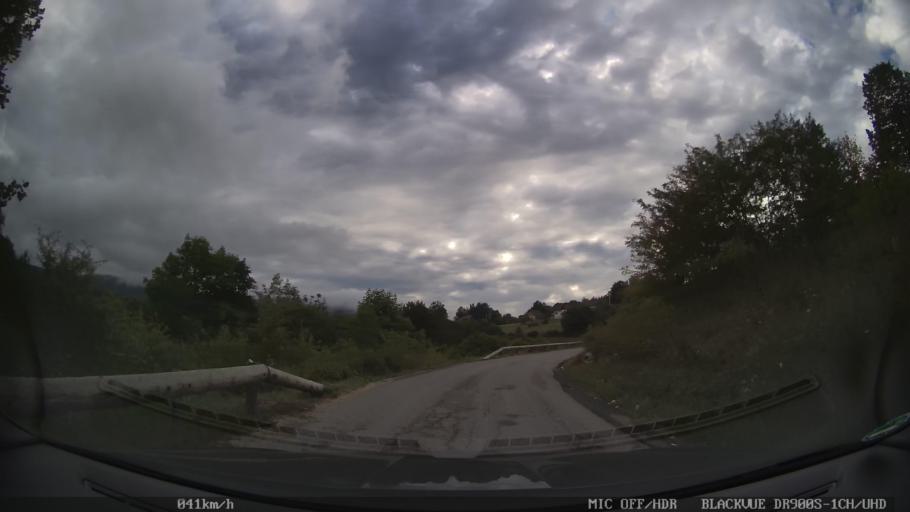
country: HR
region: Licko-Senjska
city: Jezerce
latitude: 44.9244
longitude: 15.6002
